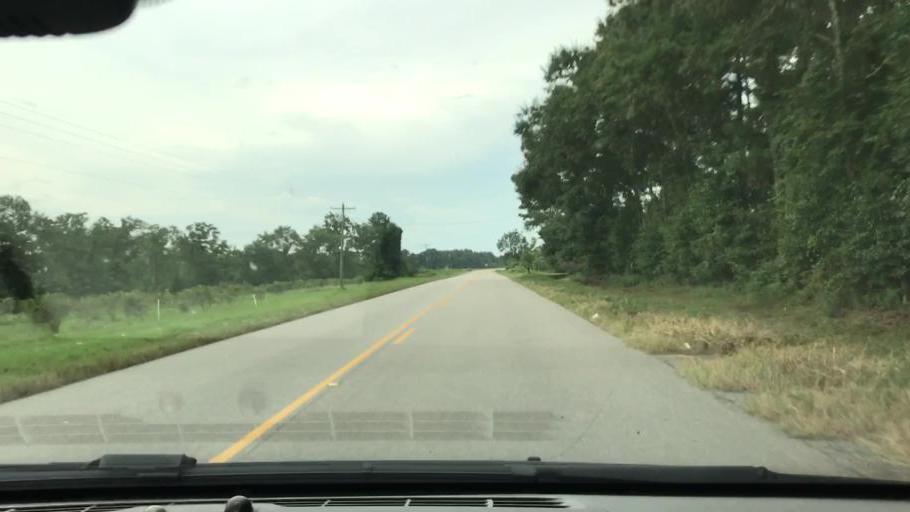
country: US
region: Alabama
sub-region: Houston County
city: Ashford
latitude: 31.2574
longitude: -85.1666
